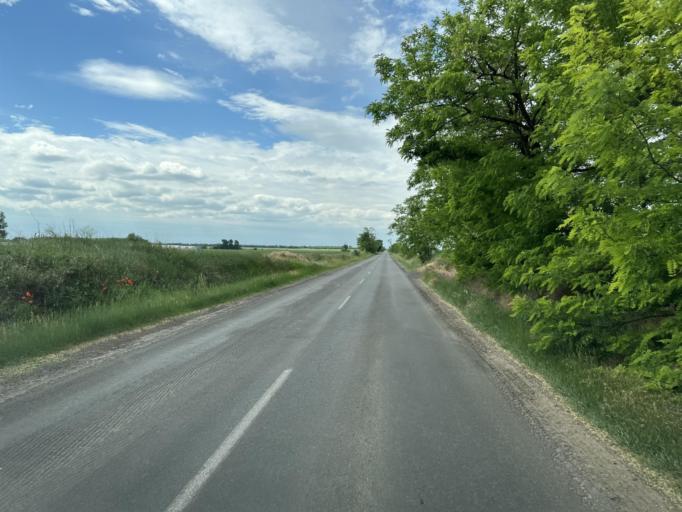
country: HU
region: Pest
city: Szentlorinckata
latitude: 47.5104
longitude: 19.7440
